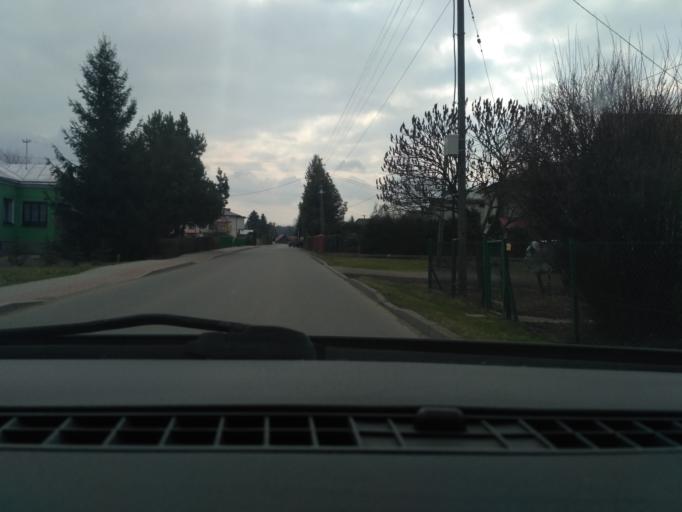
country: PL
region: Subcarpathian Voivodeship
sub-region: Powiat krosnienski
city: Kroscienko Wyzne
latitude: 49.6607
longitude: 21.8329
